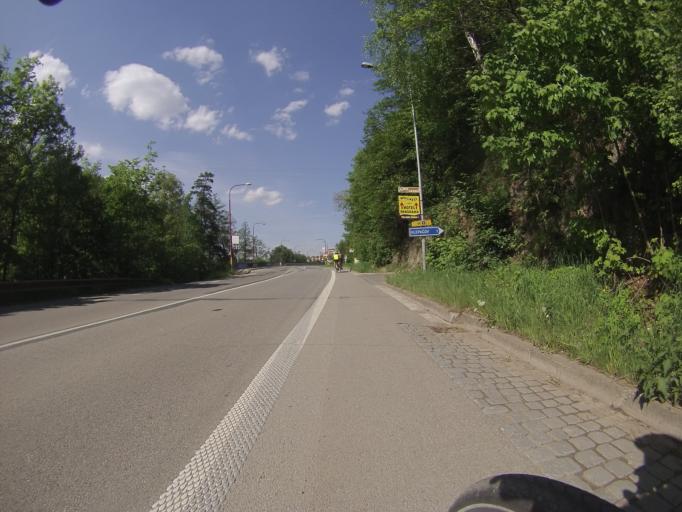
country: CZ
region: South Moravian
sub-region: Okres Blansko
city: Blansko
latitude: 49.3458
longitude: 16.6506
